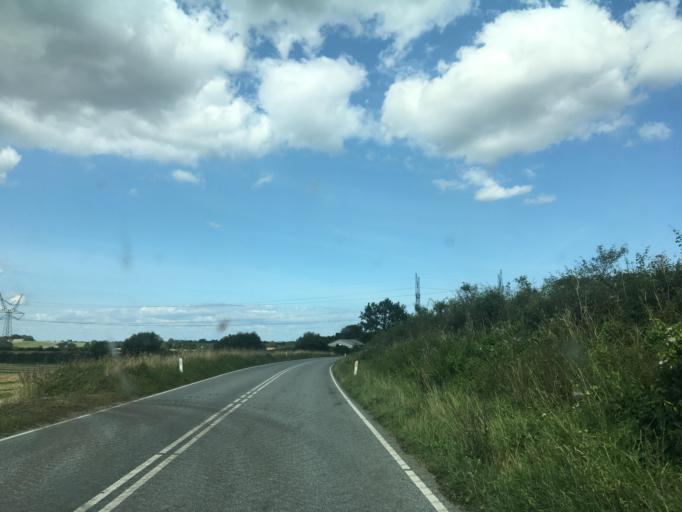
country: DK
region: South Denmark
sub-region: Middelfart Kommune
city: Ejby
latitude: 55.4165
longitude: 9.9195
